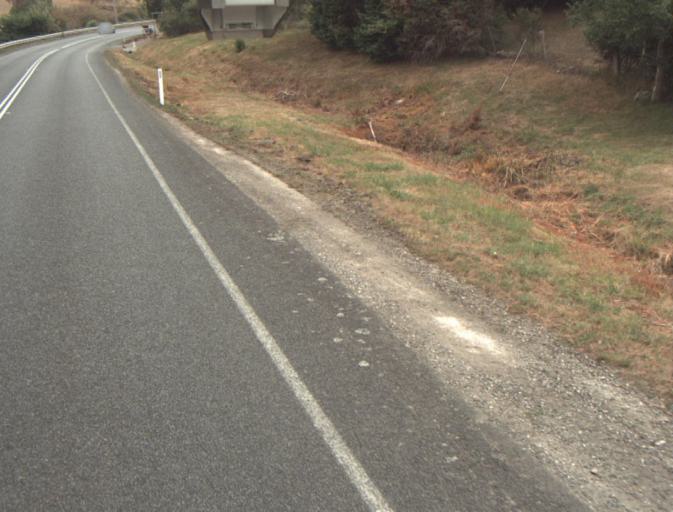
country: AU
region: Tasmania
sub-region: Launceston
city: Mayfield
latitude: -41.2695
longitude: 147.2141
